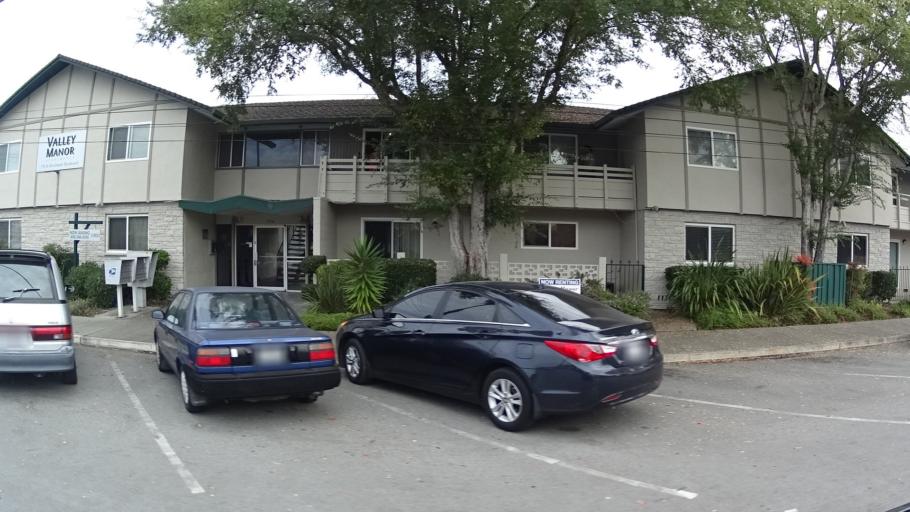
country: US
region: California
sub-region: Santa Clara County
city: Burbank
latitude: 37.3292
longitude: -121.9501
